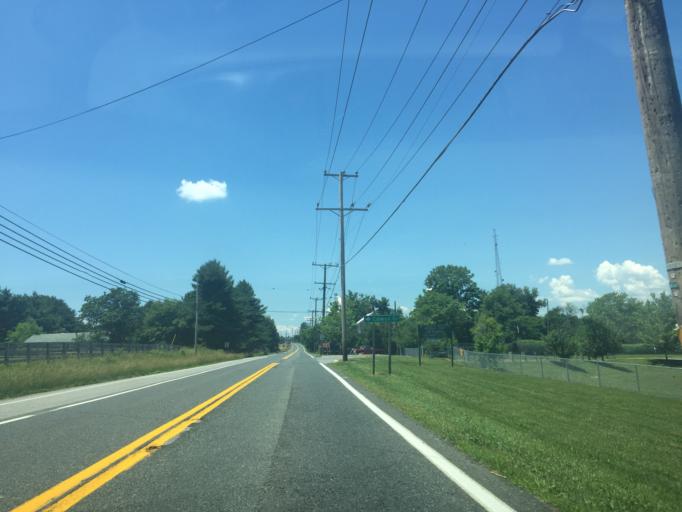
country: US
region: Maryland
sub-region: Harford County
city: Jarrettsville
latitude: 39.6129
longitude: -76.5083
